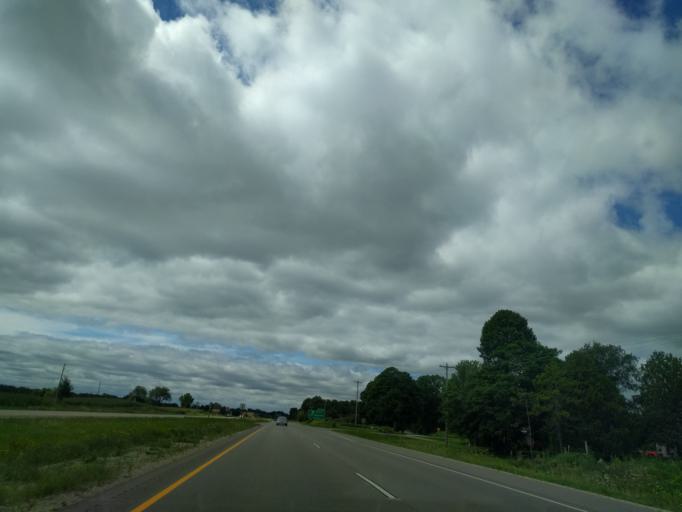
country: US
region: Wisconsin
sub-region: Oconto County
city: Oconto Falls
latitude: 44.7957
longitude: -88.0307
